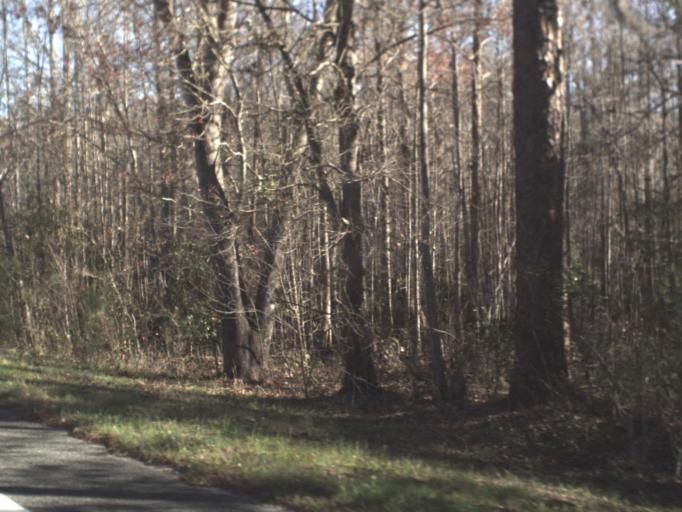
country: US
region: Georgia
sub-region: Brooks County
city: Quitman
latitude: 30.5938
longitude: -83.6416
